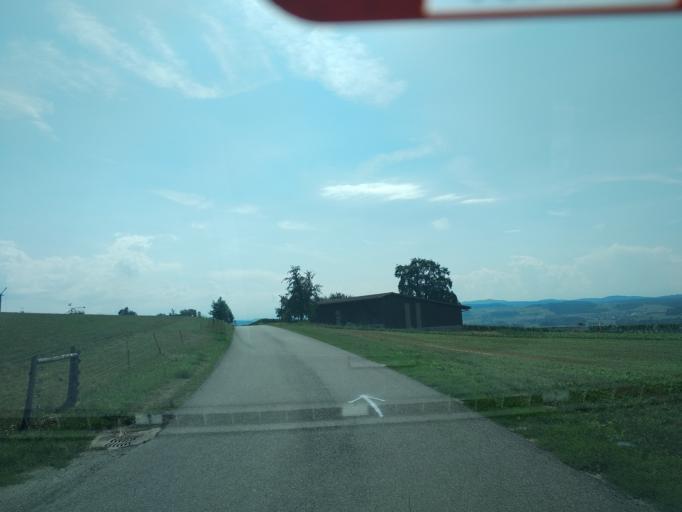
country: CH
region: Thurgau
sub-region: Frauenfeld District
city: Huttwilen
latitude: 47.5886
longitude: 8.8224
